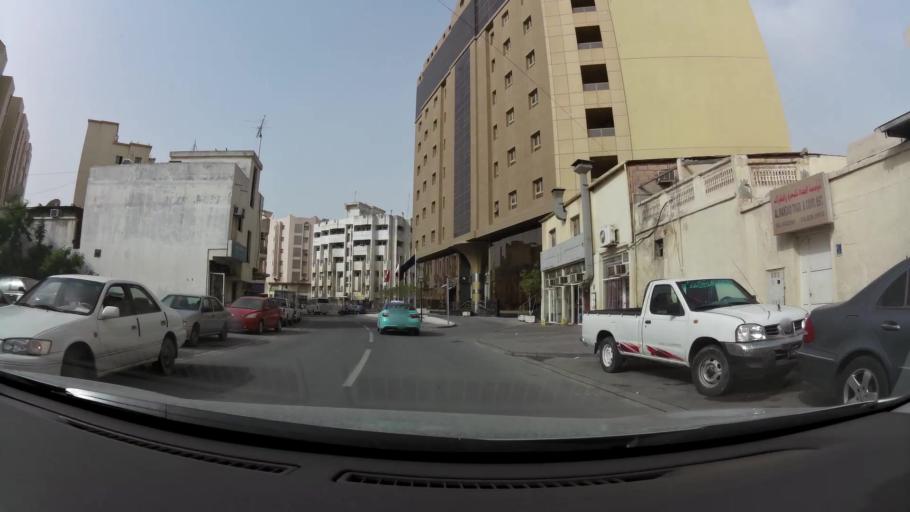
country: QA
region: Baladiyat ad Dawhah
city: Doha
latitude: 25.2805
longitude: 51.5480
